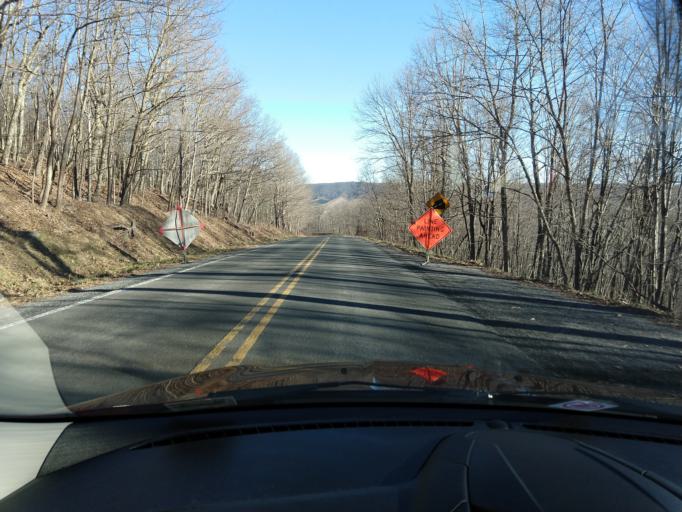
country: US
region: Virginia
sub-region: Highland County
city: Monterey
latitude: 38.4336
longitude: -79.6498
